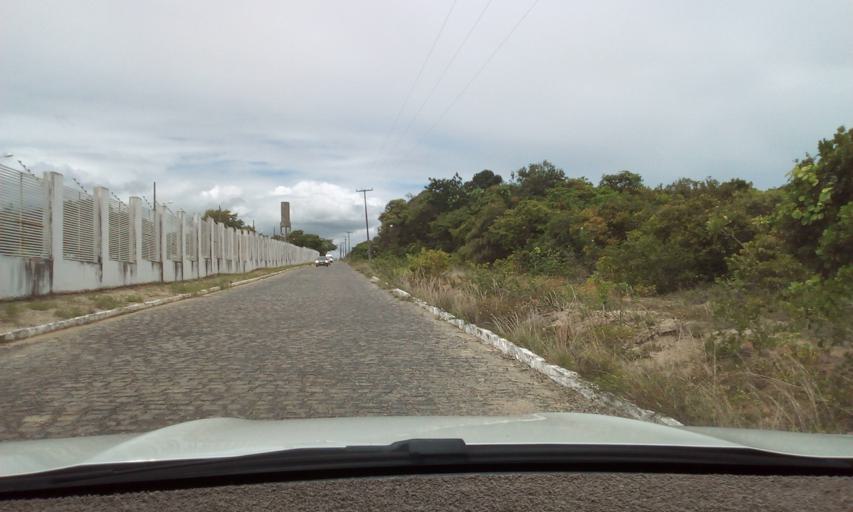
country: BR
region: Paraiba
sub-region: Conde
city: Conde
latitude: -7.3340
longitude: -34.8047
